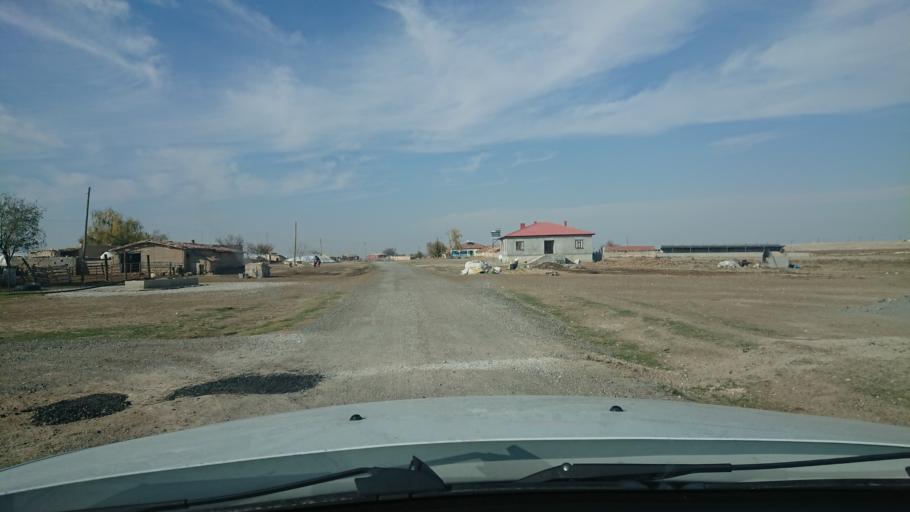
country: TR
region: Aksaray
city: Sultanhani
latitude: 38.2560
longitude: 33.4786
